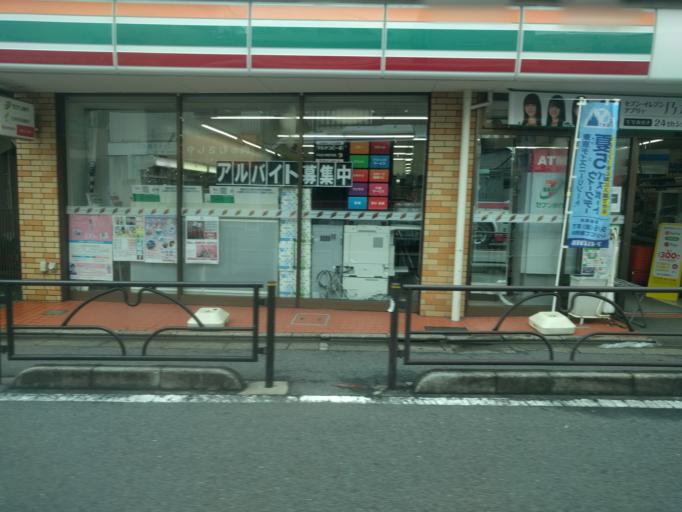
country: JP
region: Tokyo
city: Tokyo
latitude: 35.6048
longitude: 139.6717
